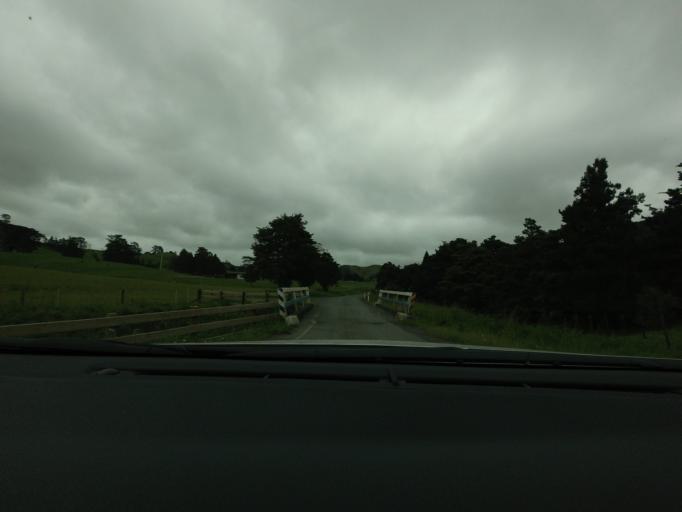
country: NZ
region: Auckland
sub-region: Auckland
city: Warkworth
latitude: -36.4792
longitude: 174.5853
